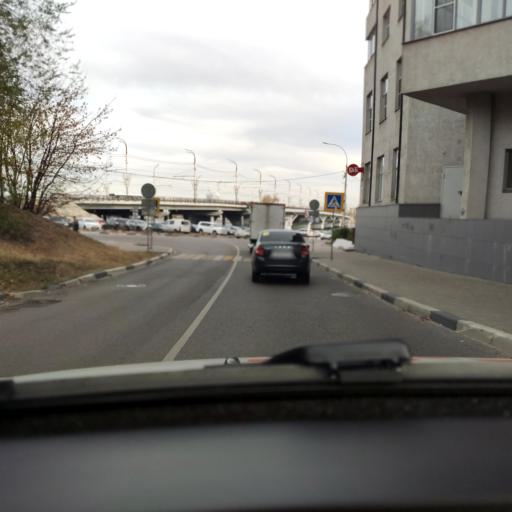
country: RU
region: Voronezj
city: Voronezh
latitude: 51.6670
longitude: 39.2194
